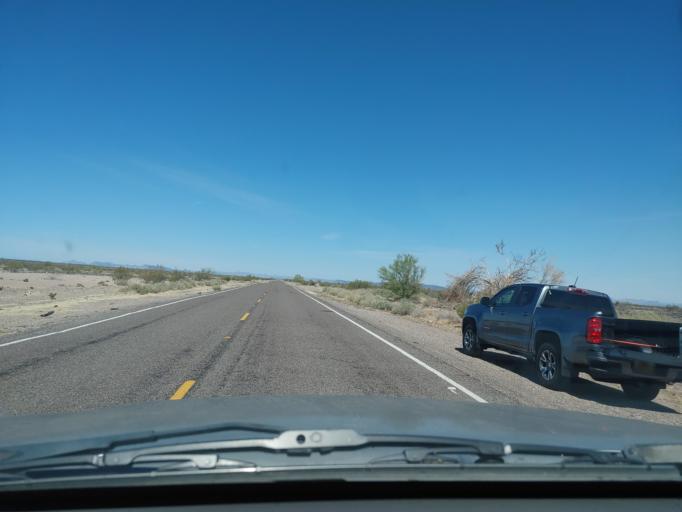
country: US
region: Arizona
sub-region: Maricopa County
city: Gila Bend
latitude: 32.8848
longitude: -113.2324
